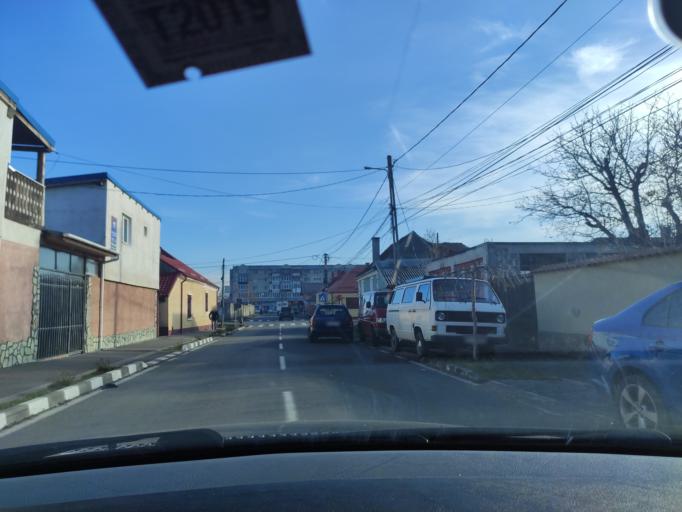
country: RO
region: Brasov
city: Codlea
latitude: 45.6927
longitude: 25.4446
